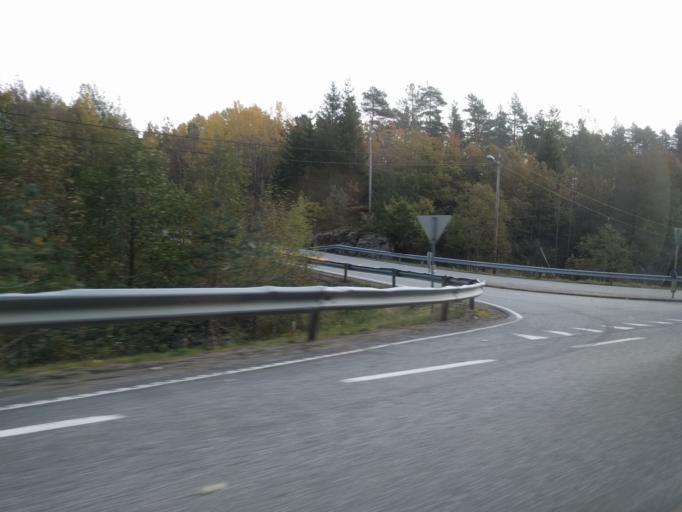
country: NO
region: Vest-Agder
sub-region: Kristiansand
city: Strai
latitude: 58.2474
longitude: 7.8712
